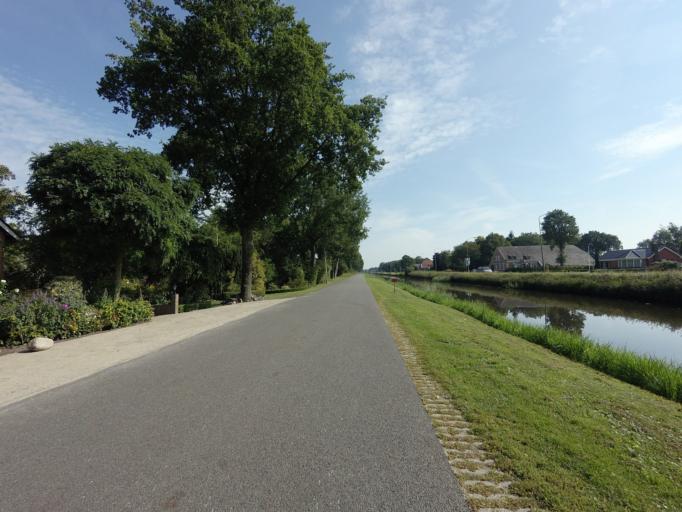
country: NL
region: Overijssel
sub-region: Gemeente Hardenberg
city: Hardenberg
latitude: 52.6407
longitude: 6.5877
